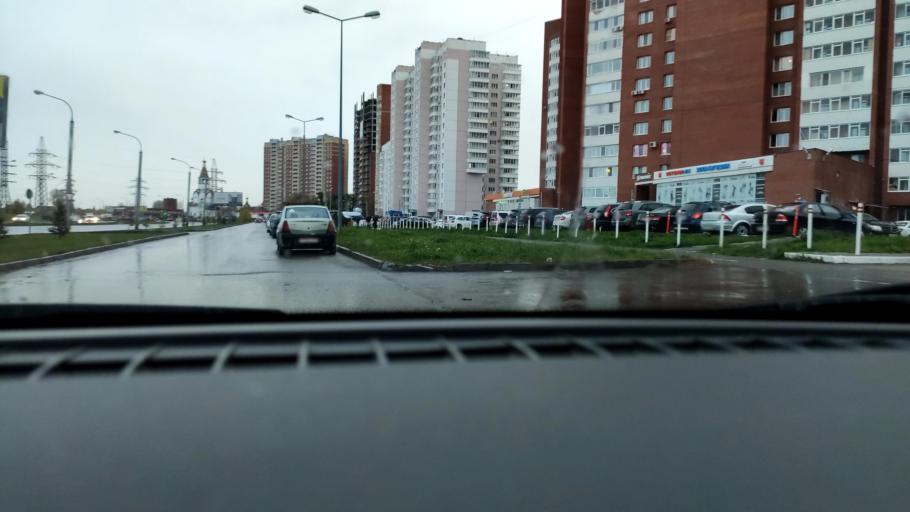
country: RU
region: Perm
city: Perm
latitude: 57.9879
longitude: 56.2872
